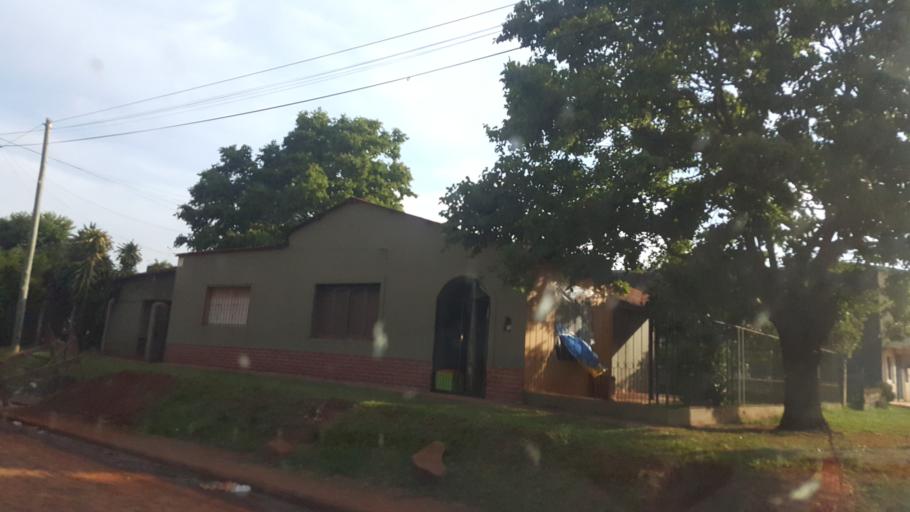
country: AR
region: Misiones
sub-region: Departamento de Capital
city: Posadas
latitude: -27.4354
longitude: -55.8833
